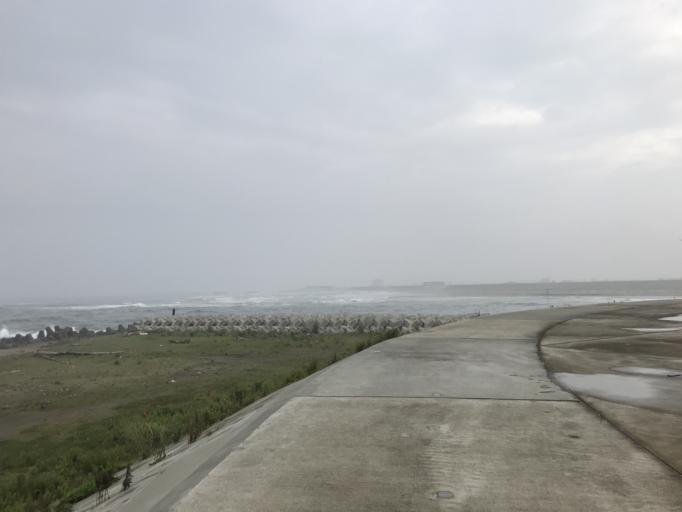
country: JP
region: Miyagi
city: Watari
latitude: 38.0511
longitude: 140.9218
